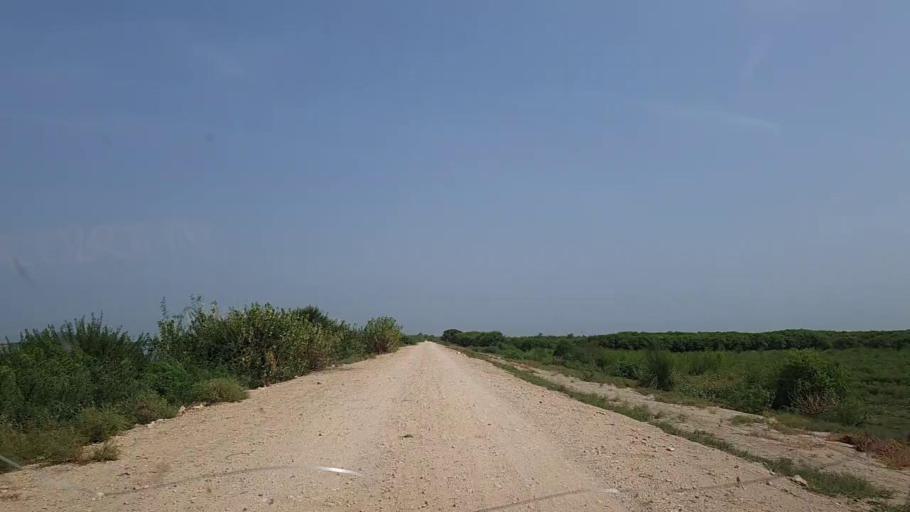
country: PK
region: Sindh
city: Ghotki
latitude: 28.1014
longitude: 69.4003
